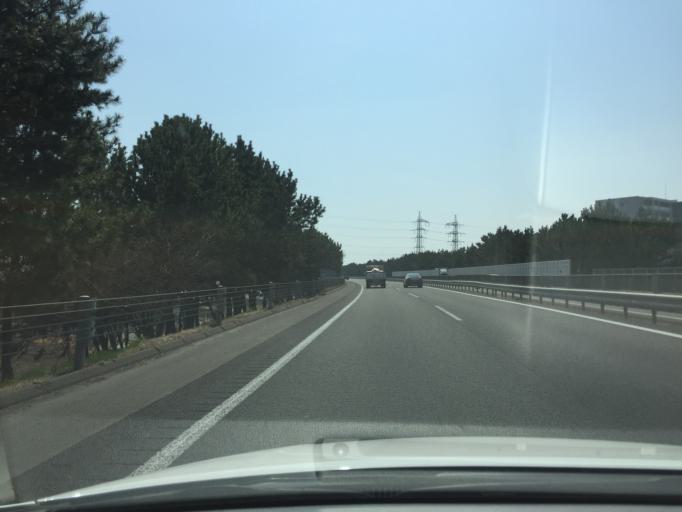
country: JP
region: Miyagi
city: Sendai-shi
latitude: 38.2384
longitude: 140.9520
